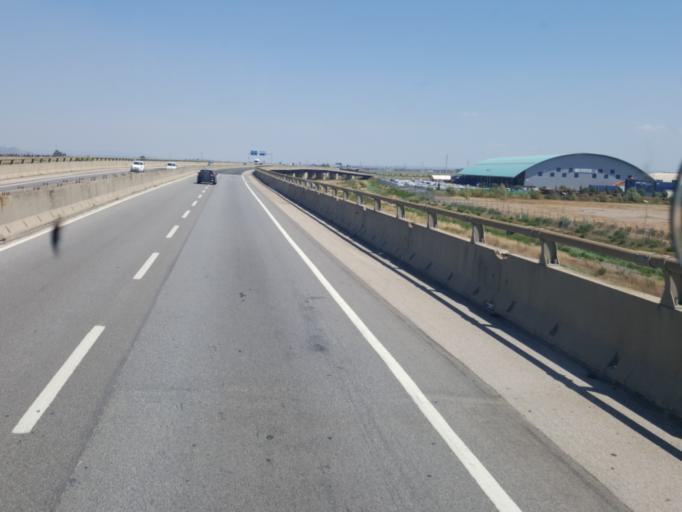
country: IT
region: Tuscany
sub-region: Provincia di Livorno
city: Guasticce
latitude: 43.6086
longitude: 10.3996
